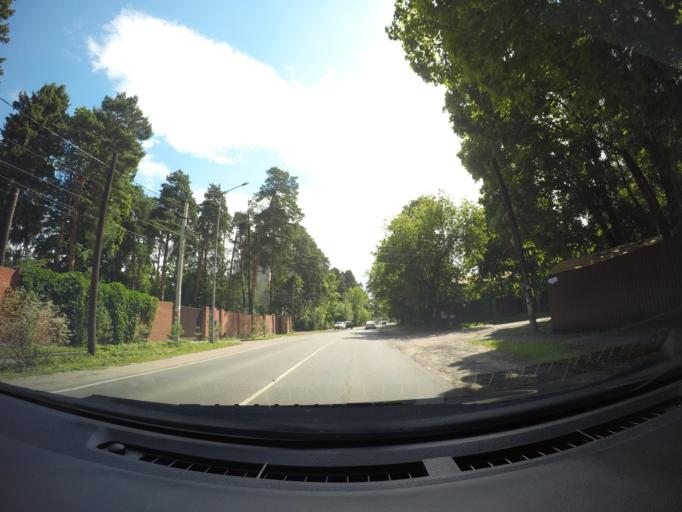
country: RU
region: Moskovskaya
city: Kraskovo
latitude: 55.6489
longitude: 38.0011
